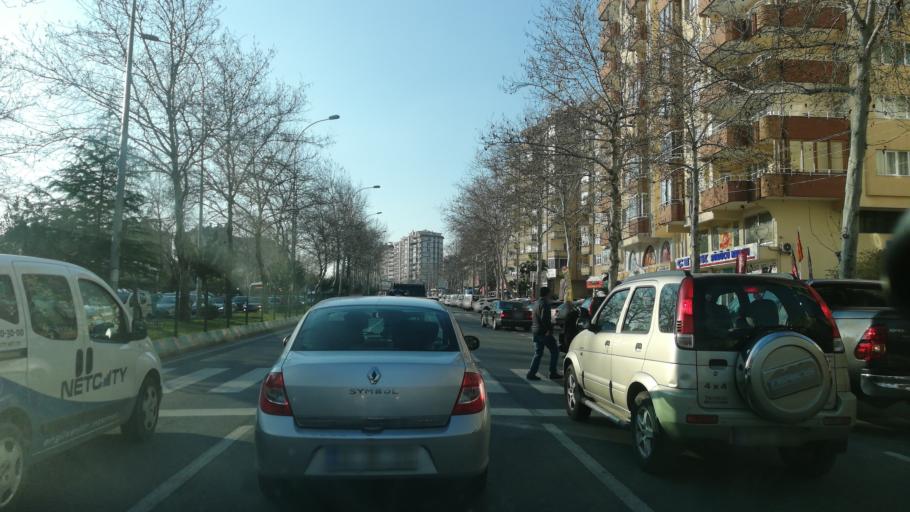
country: TR
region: Kahramanmaras
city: Kahramanmaras
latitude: 37.5858
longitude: 36.9004
